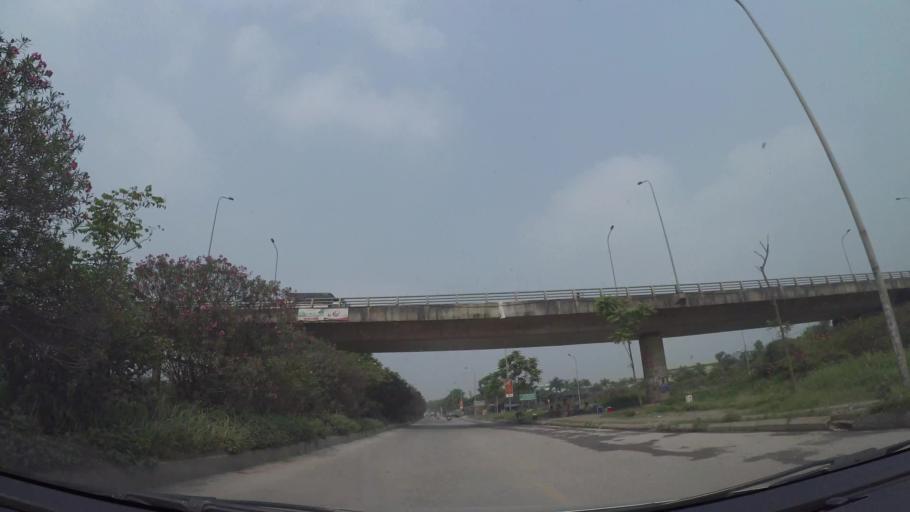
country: VN
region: Ha Noi
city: Cau Dien
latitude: 21.0116
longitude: 105.7207
